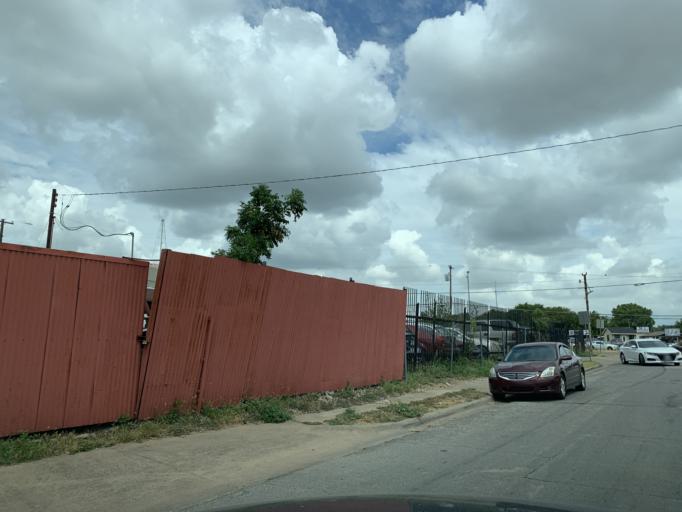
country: US
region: Texas
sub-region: Dallas County
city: Cockrell Hill
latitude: 32.7548
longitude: -96.8701
